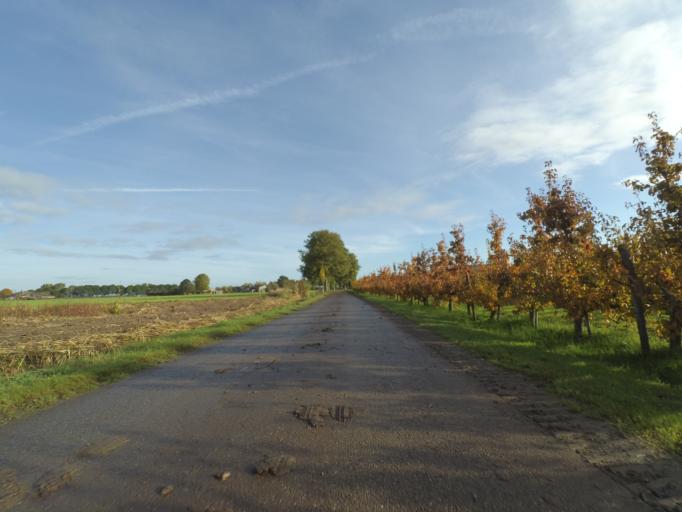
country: NL
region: Gelderland
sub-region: Gemeente Culemborg
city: Culemborg
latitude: 51.9852
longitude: 5.2795
